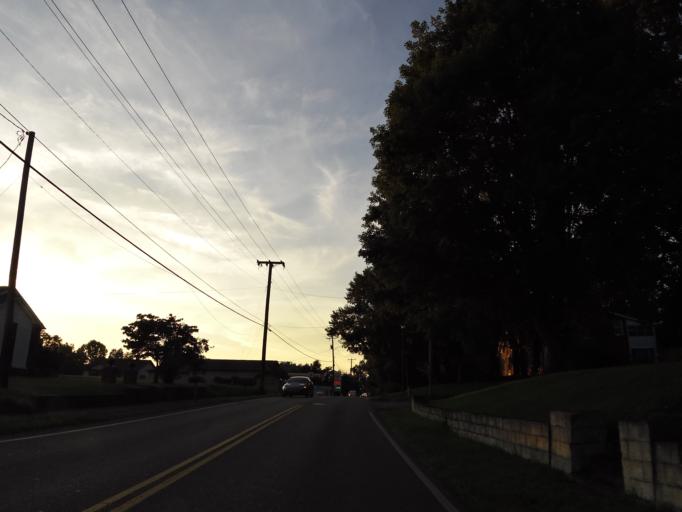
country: US
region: Tennessee
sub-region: Blount County
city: Maryville
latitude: 35.7452
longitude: -83.9691
